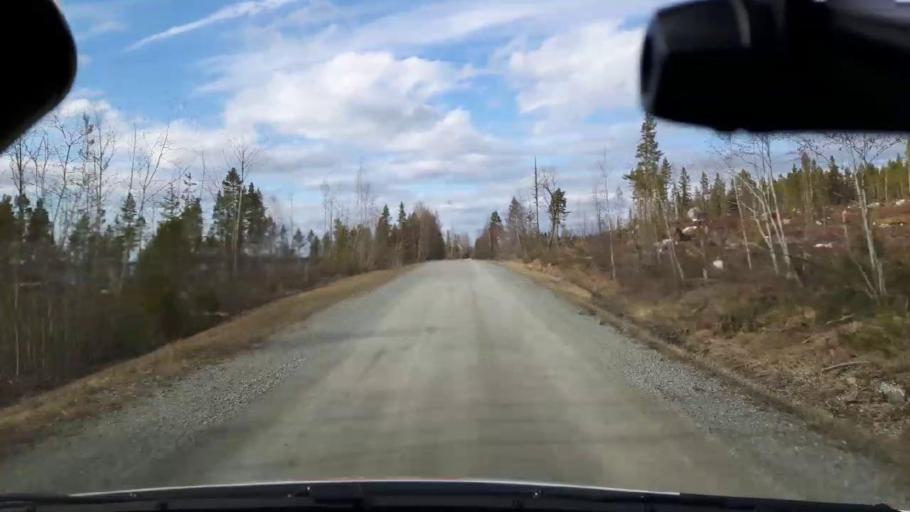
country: SE
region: Jaemtland
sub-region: Bergs Kommun
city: Hoverberg
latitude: 62.7401
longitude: 14.6636
